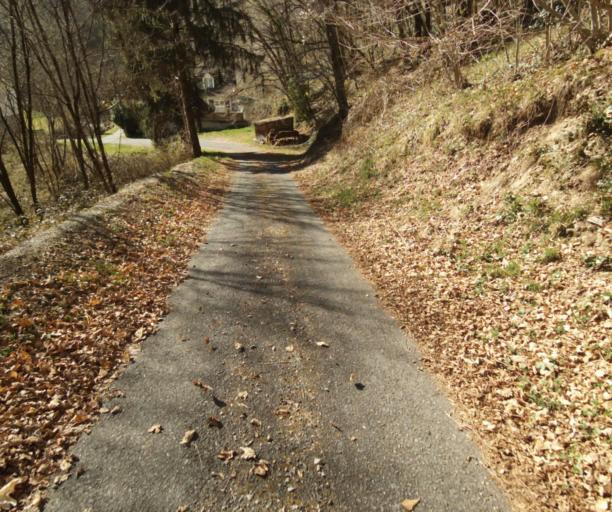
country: FR
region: Limousin
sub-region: Departement de la Correze
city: Tulle
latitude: 45.2723
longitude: 1.7427
